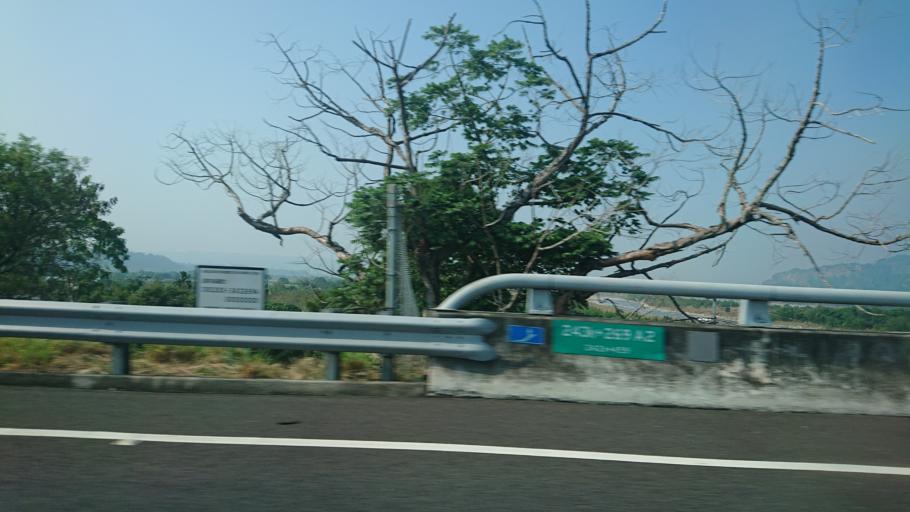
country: TW
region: Taiwan
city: Lugu
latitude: 23.8001
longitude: 120.6999
